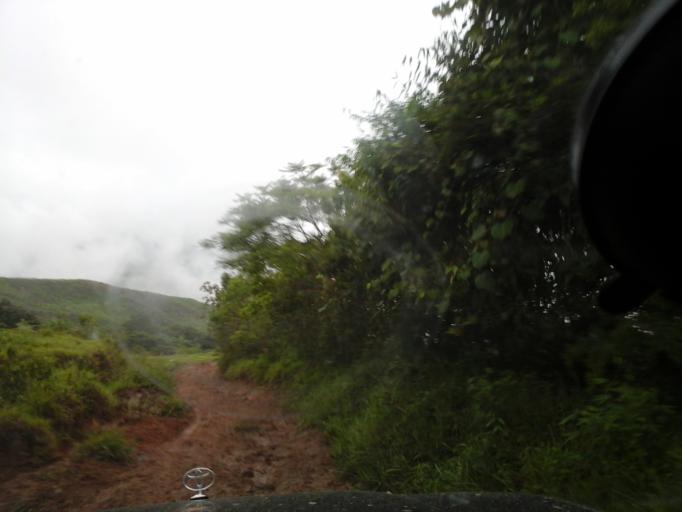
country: CO
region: Cesar
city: Agustin Codazzi
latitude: 9.9564
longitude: -73.0642
